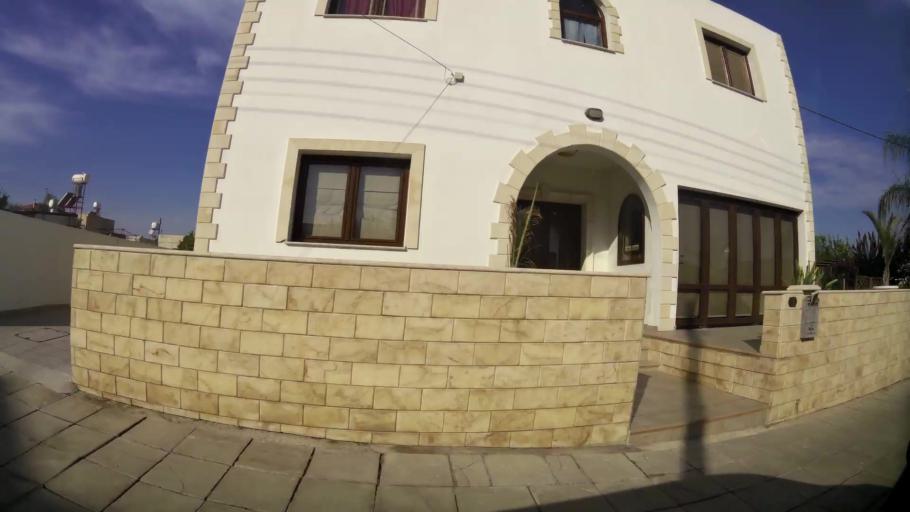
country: CY
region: Larnaka
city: Aradippou
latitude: 34.9512
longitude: 33.5956
